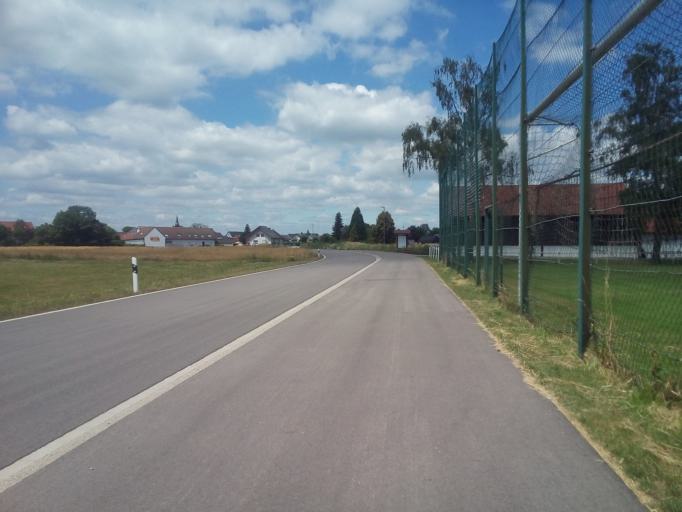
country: DE
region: Baden-Wuerttemberg
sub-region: Freiburg Region
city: Rheinau
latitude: 48.6483
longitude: 7.9366
